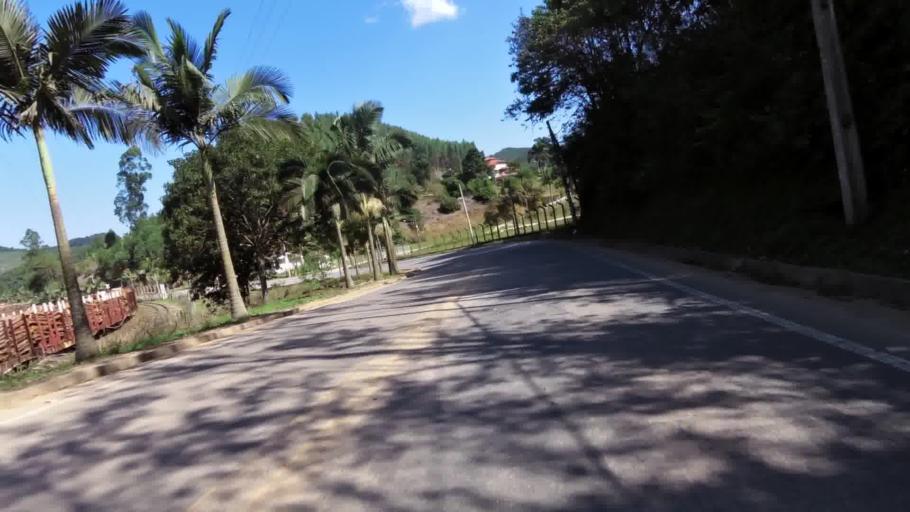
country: BR
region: Espirito Santo
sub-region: Marechal Floriano
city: Marechal Floriano
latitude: -20.4794
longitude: -40.7708
